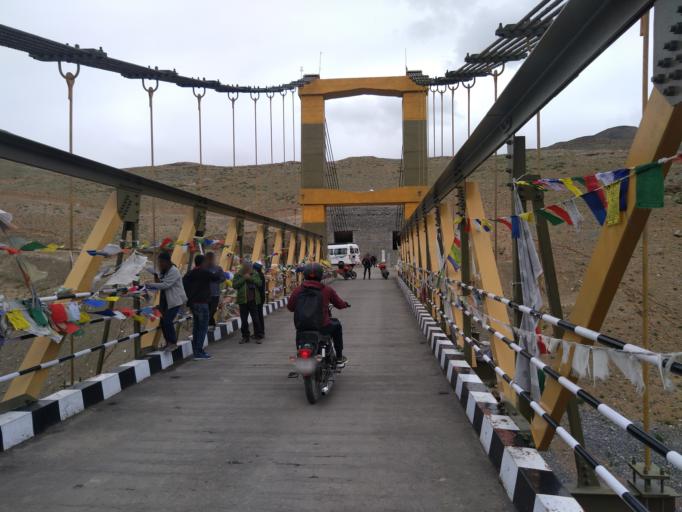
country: IN
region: Himachal Pradesh
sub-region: Kulu
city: Manali
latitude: 32.3435
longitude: 77.9974
